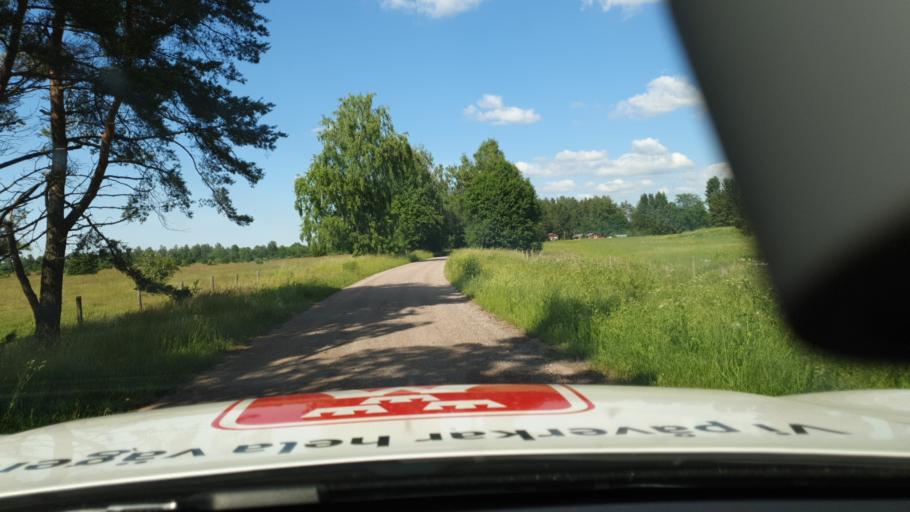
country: SE
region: Vaestra Goetaland
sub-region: Skara Kommun
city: Axvall
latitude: 58.3935
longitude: 13.5926
